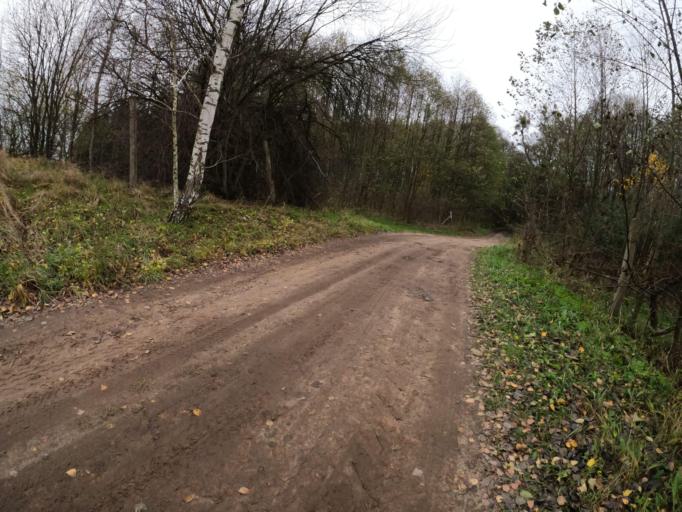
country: PL
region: West Pomeranian Voivodeship
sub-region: Powiat walecki
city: Miroslawiec
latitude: 53.2890
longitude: 16.1416
